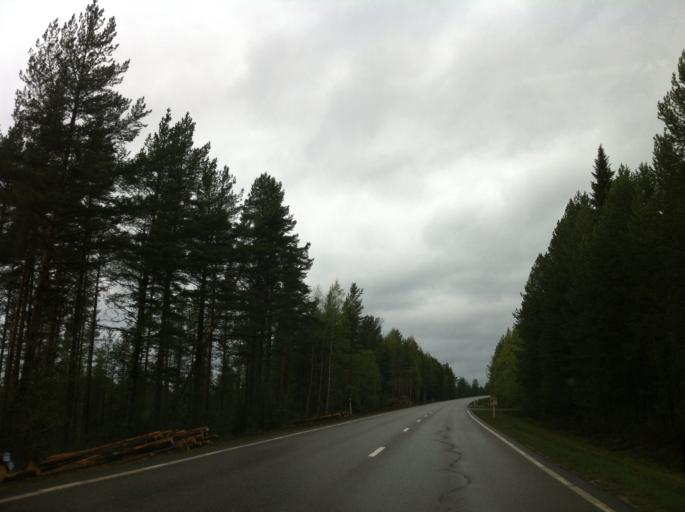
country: SE
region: Jaemtland
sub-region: Harjedalens Kommun
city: Sveg
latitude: 62.0486
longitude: 14.3218
